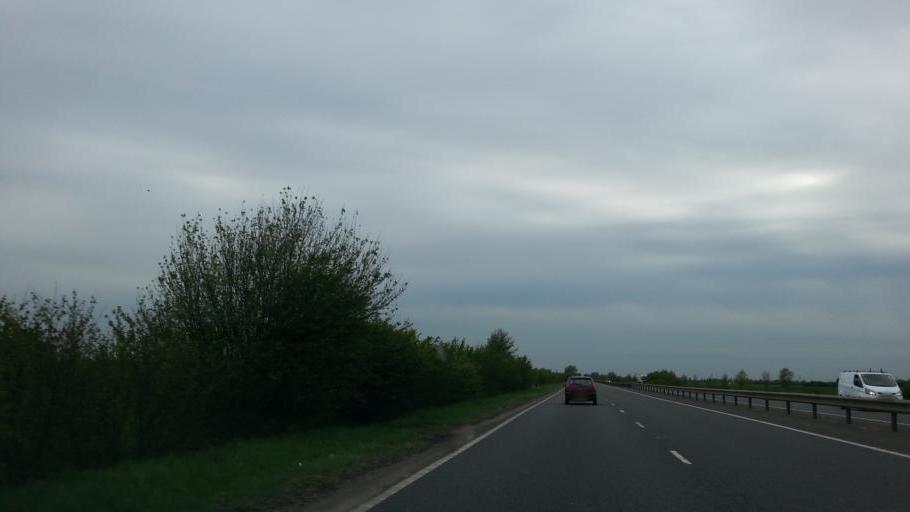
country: GB
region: England
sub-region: Peterborough
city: Thorney
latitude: 52.6230
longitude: -0.0758
